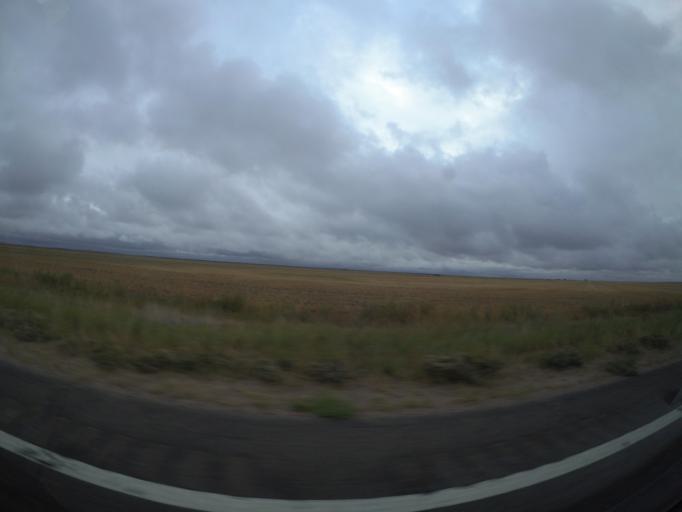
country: US
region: Colorado
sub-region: Washington County
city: Akron
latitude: 39.7283
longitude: -103.1620
